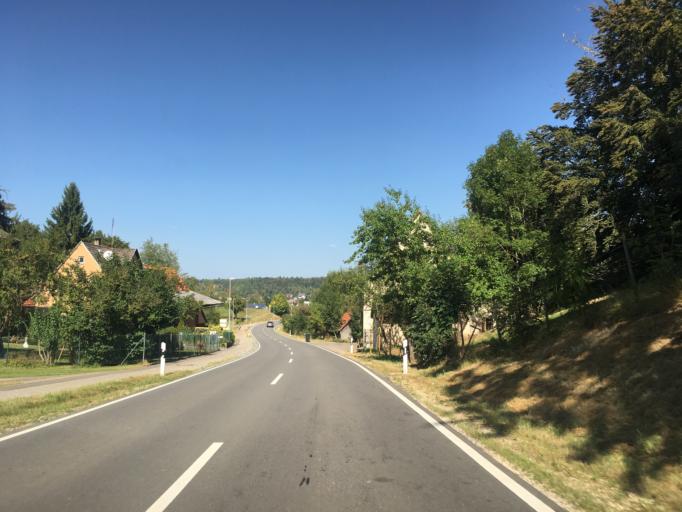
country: DE
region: Baden-Wuerttemberg
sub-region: Tuebingen Region
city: Munsingen
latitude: 48.3997
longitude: 9.4879
